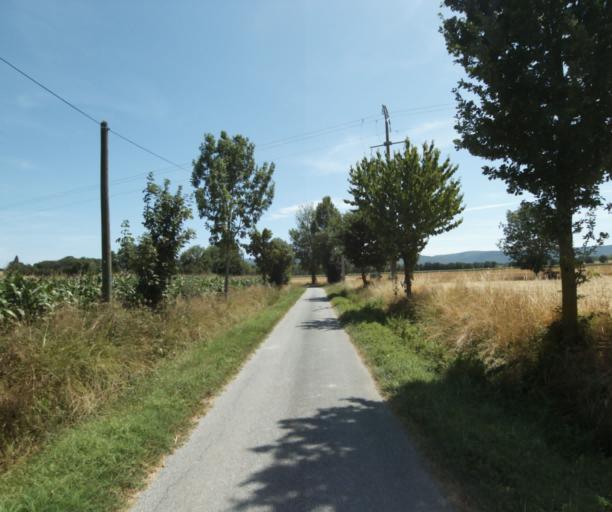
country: FR
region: Midi-Pyrenees
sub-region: Departement de la Haute-Garonne
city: Revel
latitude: 43.5025
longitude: 2.0373
